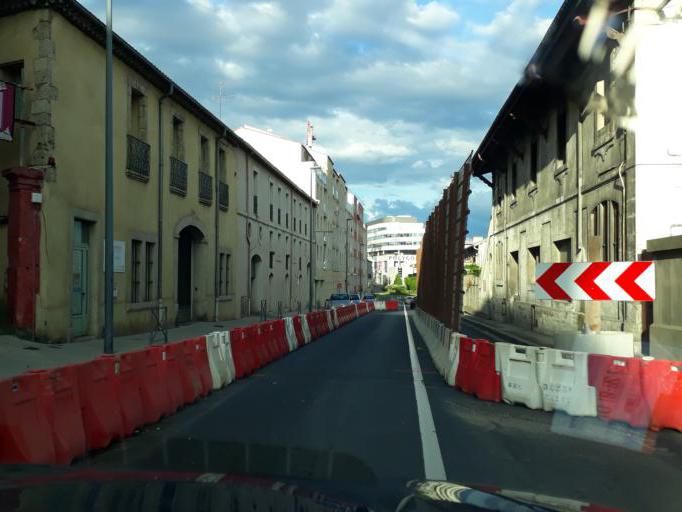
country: FR
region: Languedoc-Roussillon
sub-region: Departement de l'Herault
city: Beziers
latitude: 43.3366
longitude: 3.2202
